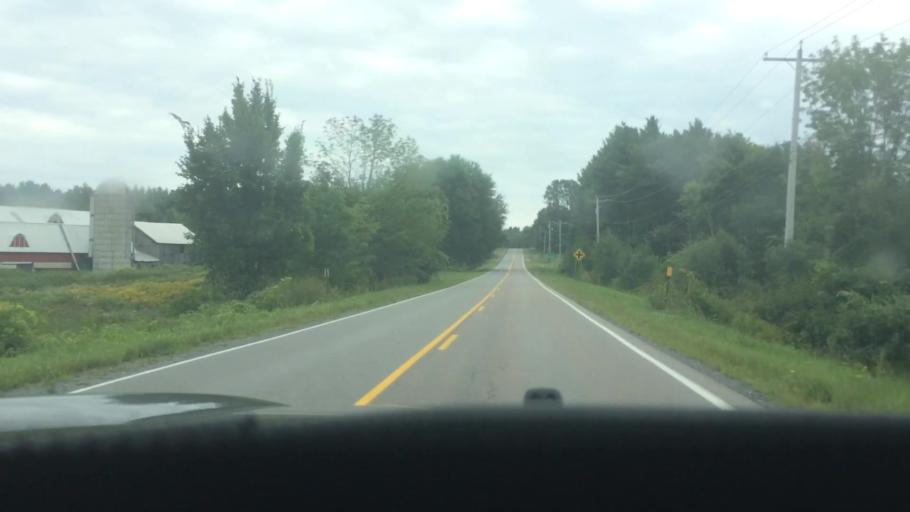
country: US
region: New York
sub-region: St. Lawrence County
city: Hannawa Falls
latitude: 44.5378
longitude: -75.0216
